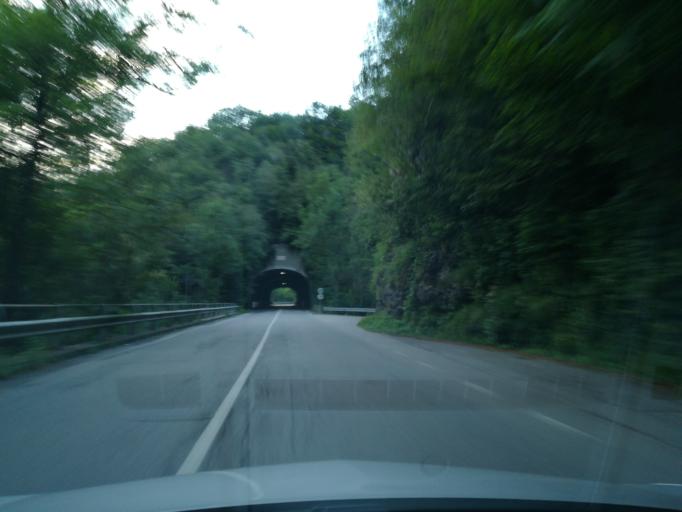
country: IT
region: Lombardy
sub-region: Provincia di Bergamo
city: Sant'Omobono Terme
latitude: 45.8025
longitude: 9.5446
